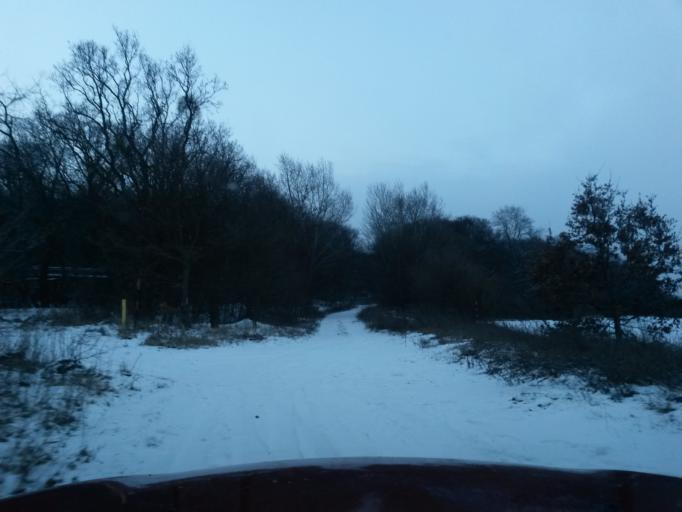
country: SK
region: Kosicky
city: Kosice
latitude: 48.7336
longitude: 21.3263
